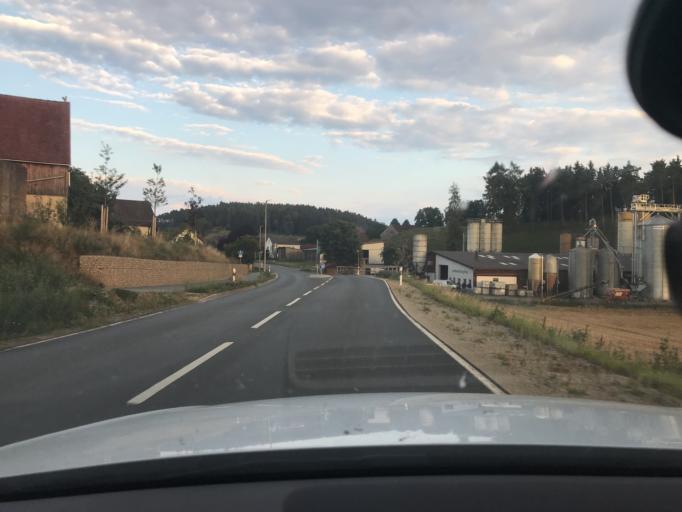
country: DE
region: Bavaria
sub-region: Upper Palatinate
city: Auerbach
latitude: 49.7231
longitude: 11.6152
